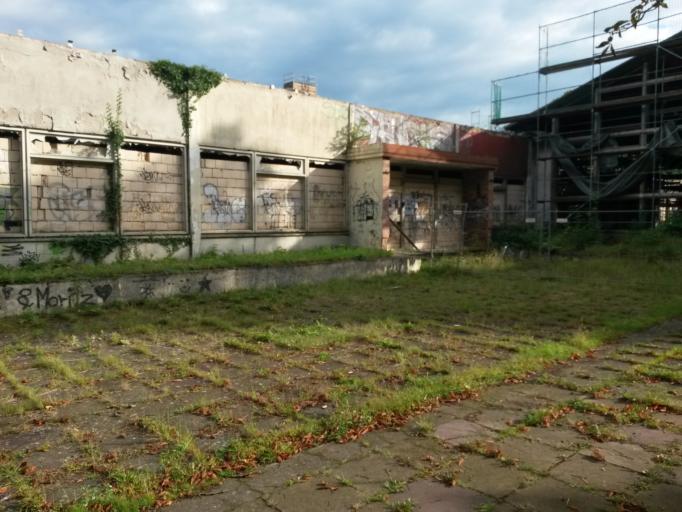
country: DE
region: Brandenburg
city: Templin
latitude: 53.1213
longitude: 13.4923
